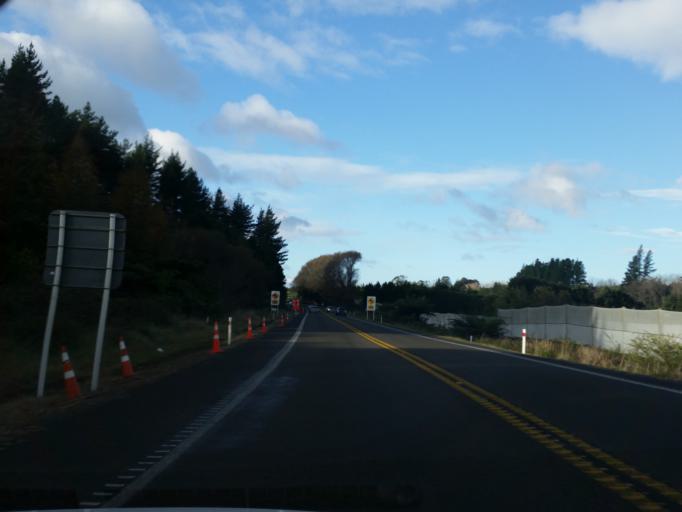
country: NZ
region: Bay of Plenty
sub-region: Western Bay of Plenty District
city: Katikati
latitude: -37.6487
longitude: 175.9783
